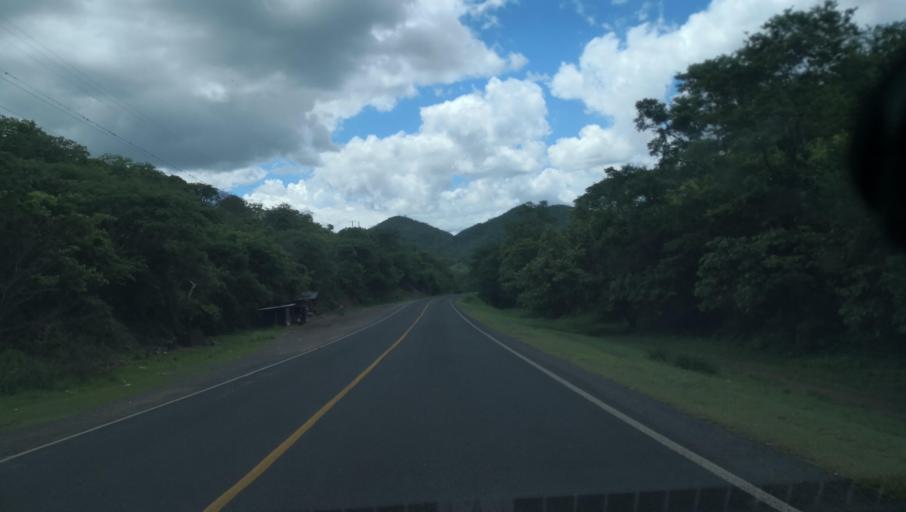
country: NI
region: Madriz
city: Palacaguina
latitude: 13.4470
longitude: -86.4426
